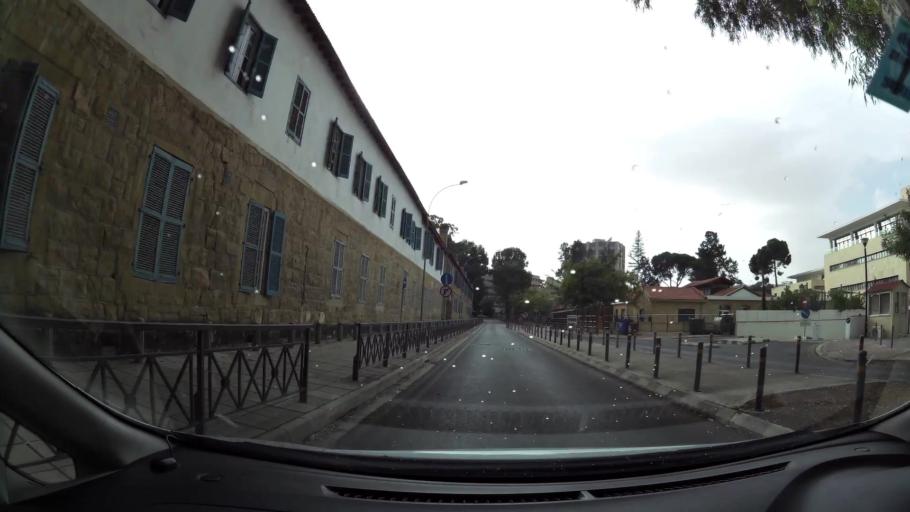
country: CY
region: Lefkosia
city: Nicosia
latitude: 35.1667
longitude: 33.3543
